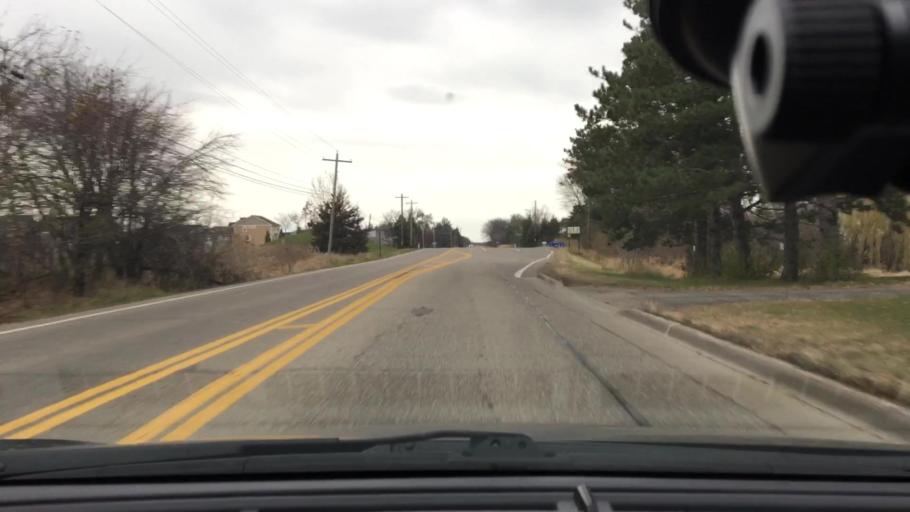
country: US
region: Minnesota
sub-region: Hennepin County
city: Corcoran
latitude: 45.0711
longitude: -93.5221
